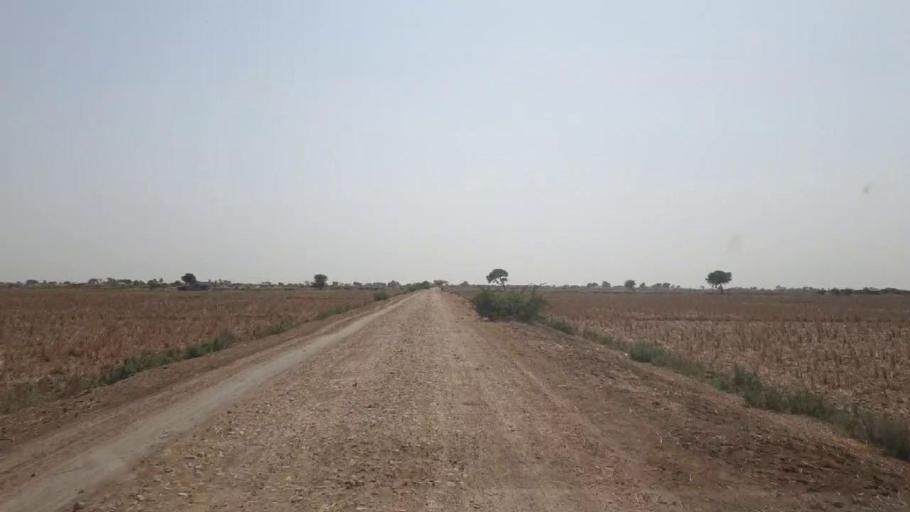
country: PK
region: Sindh
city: Jati
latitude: 24.4335
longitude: 68.5523
